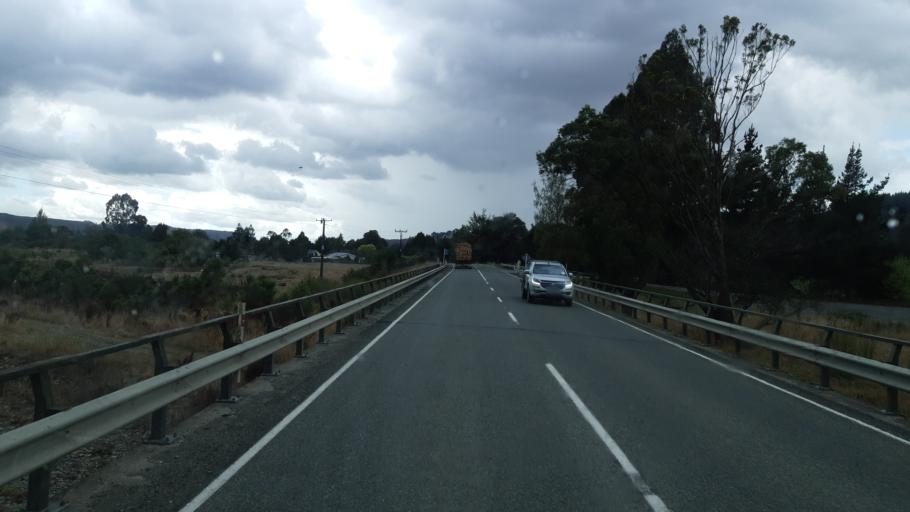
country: NZ
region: Tasman
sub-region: Tasman District
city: Wakefield
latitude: -41.4282
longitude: 172.9906
